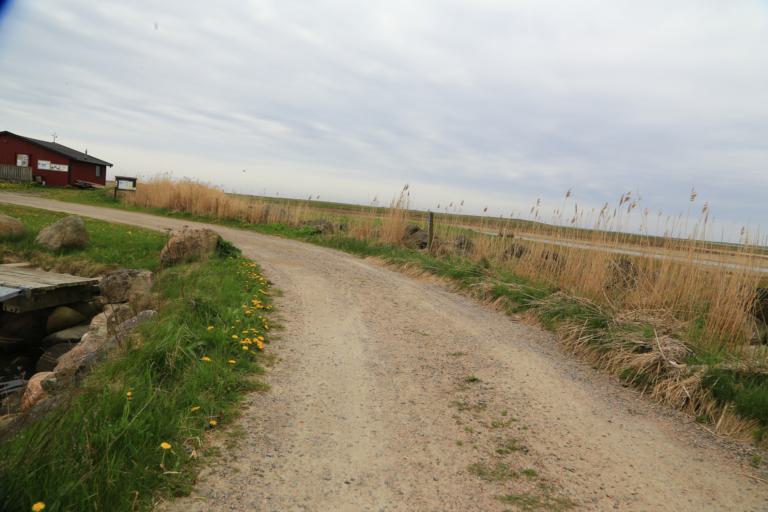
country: SE
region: Halland
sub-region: Varbergs Kommun
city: Traslovslage
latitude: 57.0288
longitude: 12.3107
